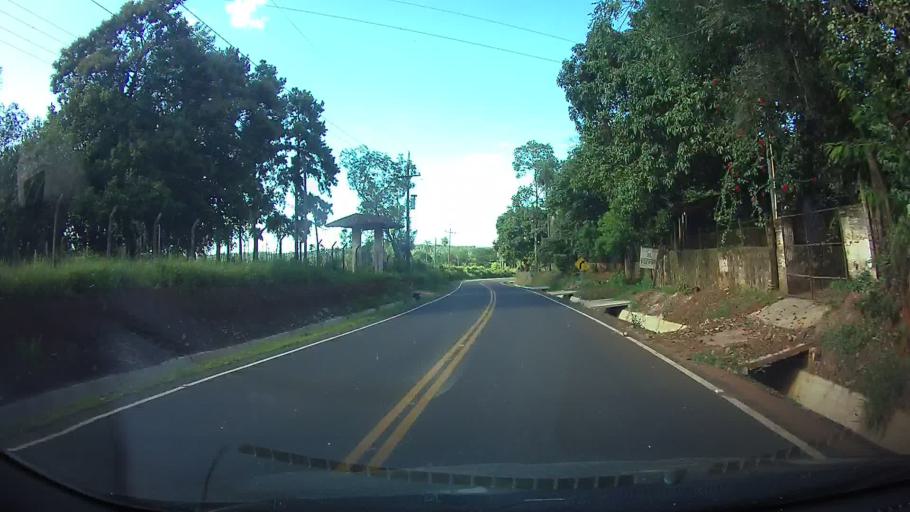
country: PY
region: Cordillera
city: Caacupe
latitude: -25.3615
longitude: -57.1473
